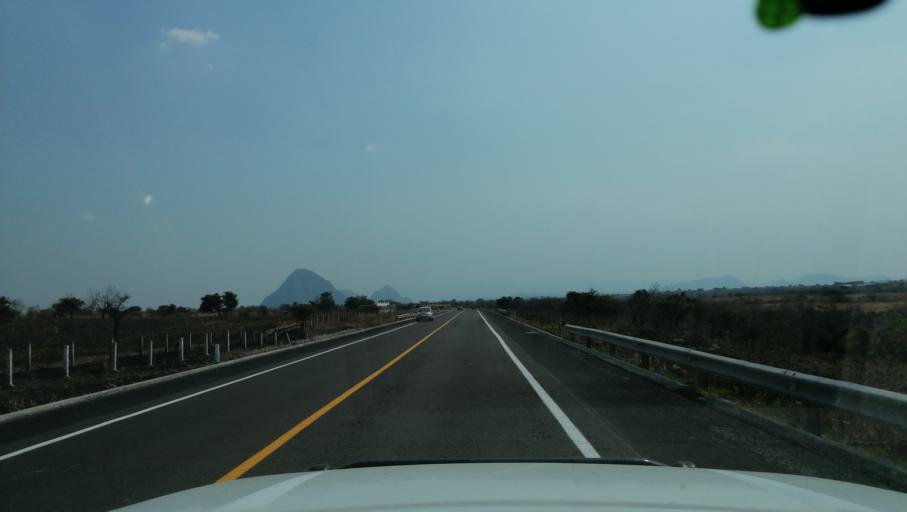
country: MX
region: Morelos
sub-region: Zacualpan
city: Zacualpan de Amilpas
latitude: 18.7725
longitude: -98.7363
